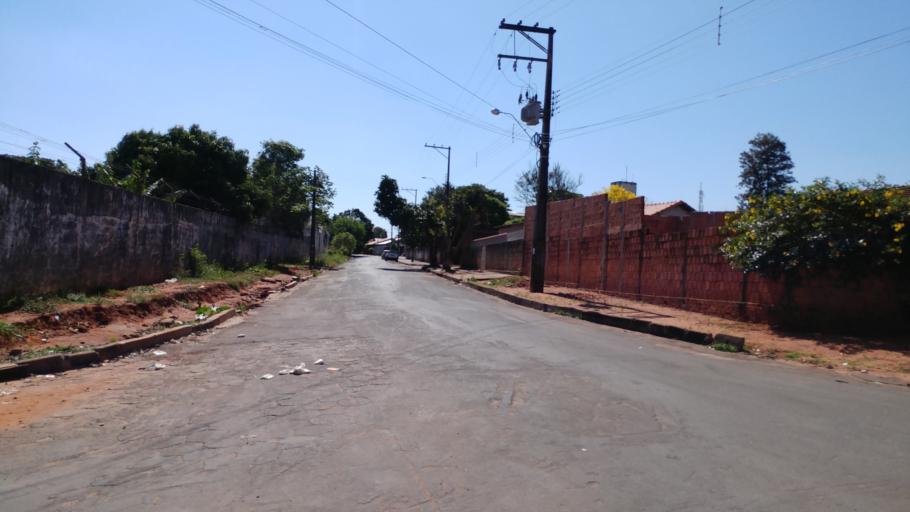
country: BR
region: Sao Paulo
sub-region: Paraguacu Paulista
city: Paraguacu Paulista
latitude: -22.4357
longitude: -50.5827
